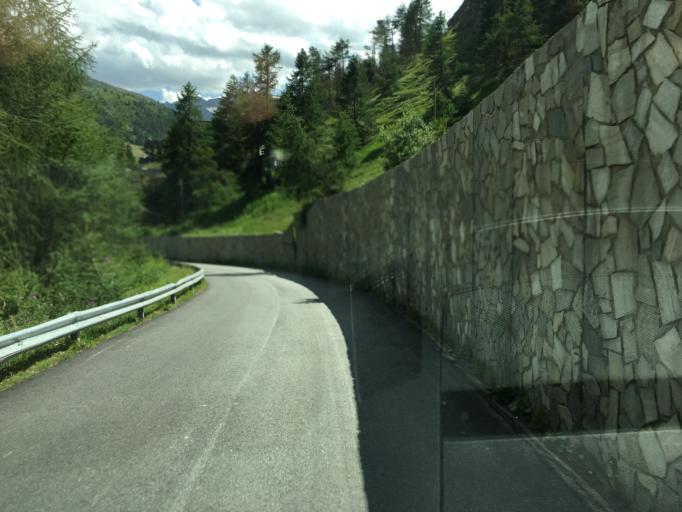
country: IT
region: Piedmont
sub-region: Provincia di Torino
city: Sestriere
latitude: 44.9637
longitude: 6.8826
